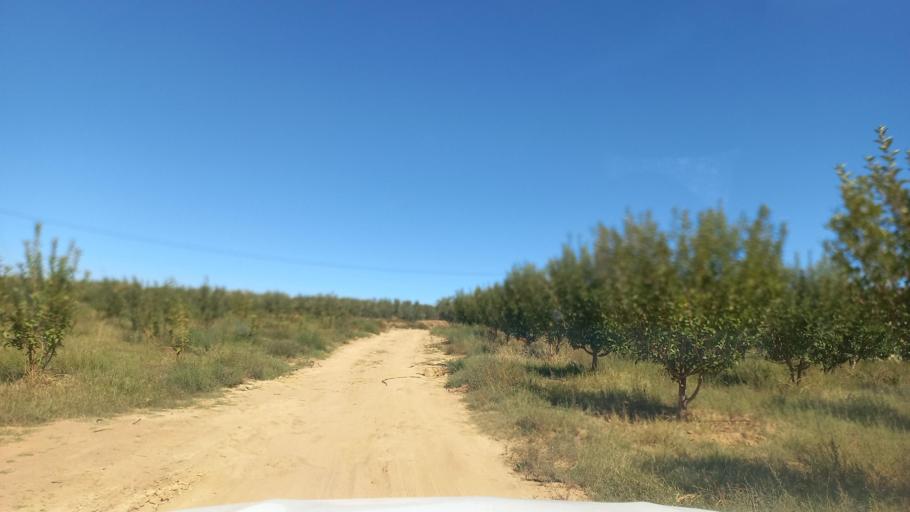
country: TN
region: Al Qasrayn
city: Sbiba
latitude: 35.3462
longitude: 9.0974
